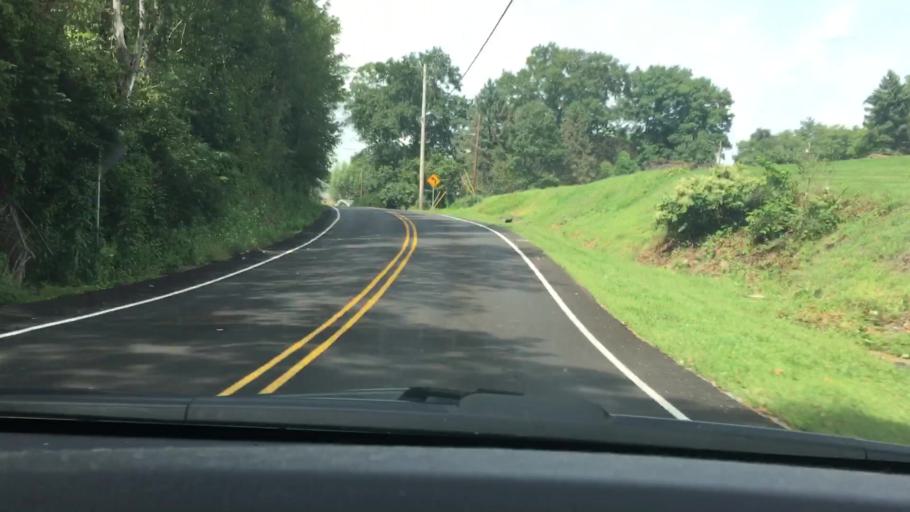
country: US
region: Pennsylvania
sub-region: Allegheny County
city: Versailles
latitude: 40.2923
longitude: -79.8390
